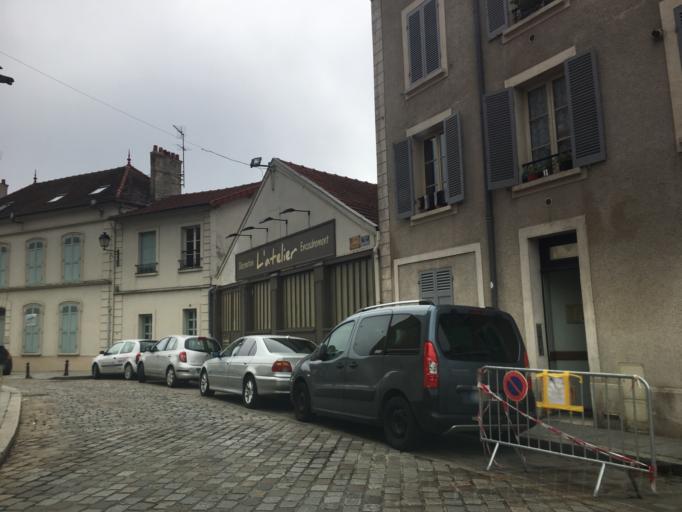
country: FR
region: Ile-de-France
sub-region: Departement de Seine-et-Marne
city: Brie-Comte-Robert
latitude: 48.6902
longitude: 2.6081
